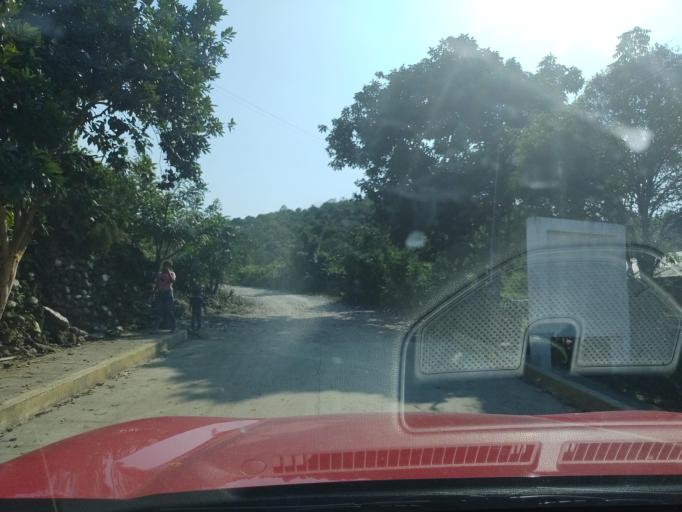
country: MX
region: Veracruz
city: Agua Dulce
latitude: 20.3483
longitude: -97.1771
